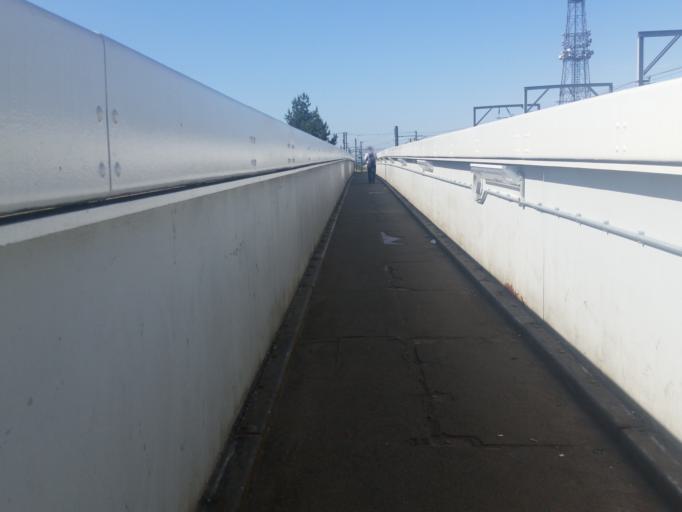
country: GB
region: England
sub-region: Greater London
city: Acton
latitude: 51.5316
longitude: -0.2436
